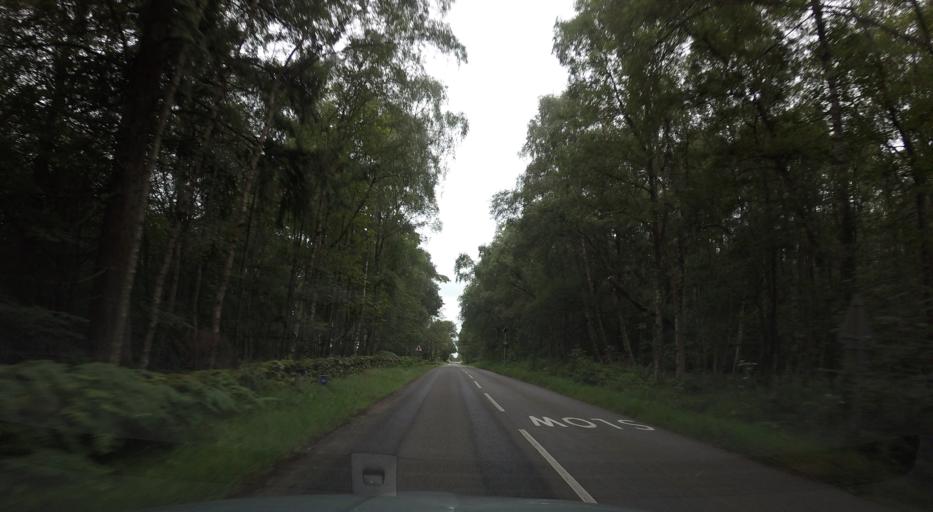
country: GB
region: Scotland
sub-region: Aberdeenshire
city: Banchory
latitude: 57.0410
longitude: -2.4988
